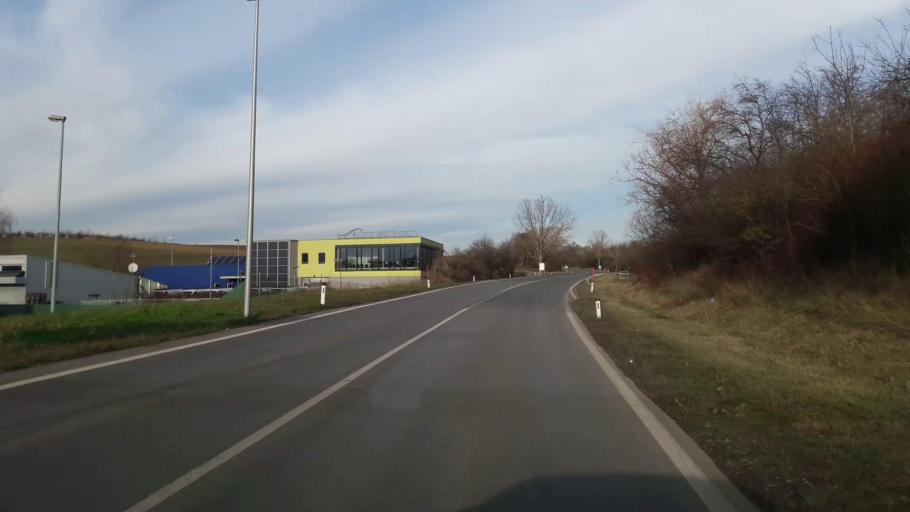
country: AT
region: Lower Austria
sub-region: Politischer Bezirk Mistelbach
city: Gaweinstal
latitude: 48.4845
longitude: 16.5933
